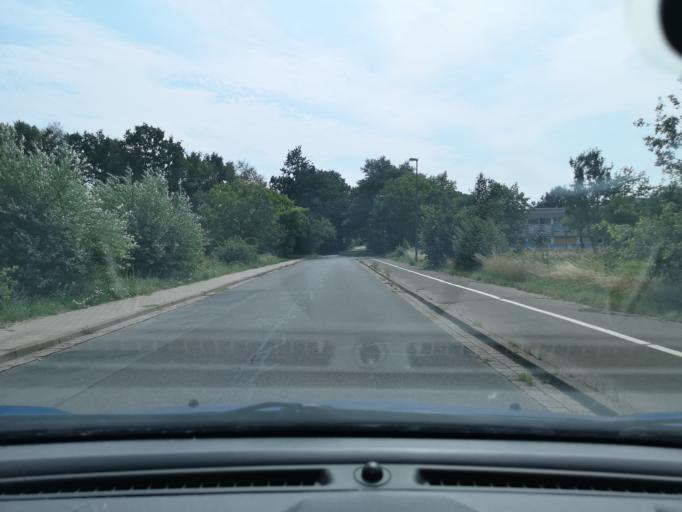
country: DE
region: Lower Saxony
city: Langenhagen
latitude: 52.4343
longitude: 9.6996
